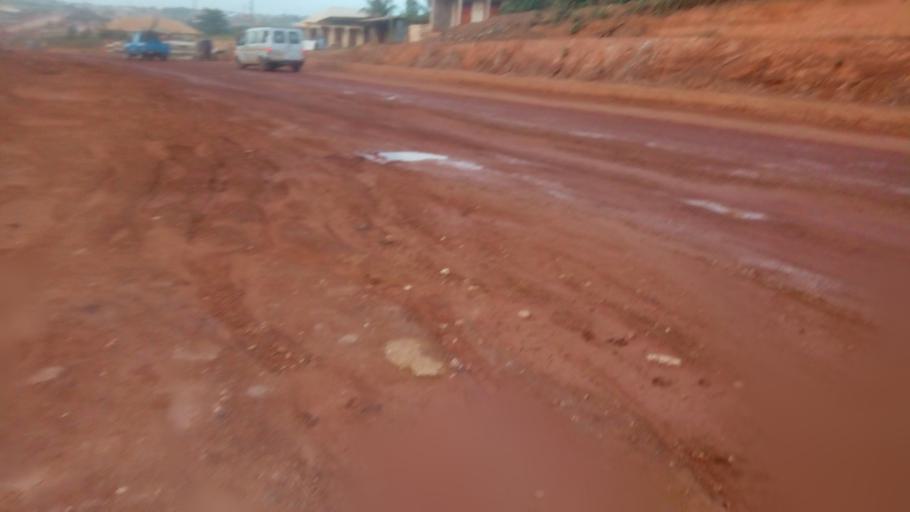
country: GH
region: Ashanti
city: Obuasi
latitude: 6.2233
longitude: -1.6838
